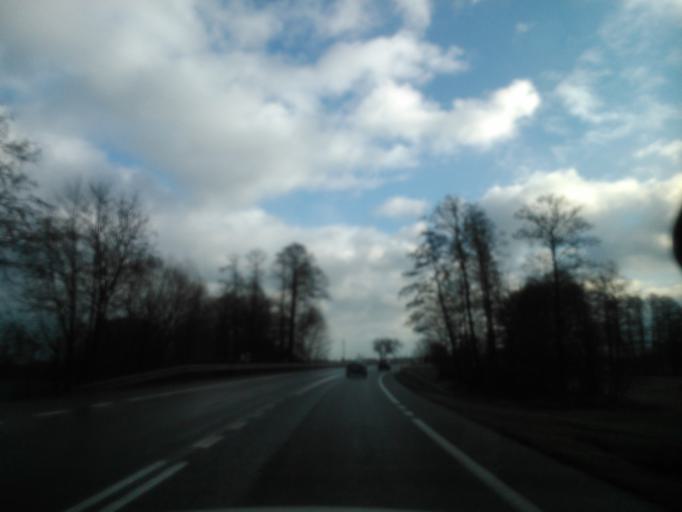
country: PL
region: Masovian Voivodeship
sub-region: Powiat sierpecki
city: Rosciszewo
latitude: 52.8242
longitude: 19.7714
